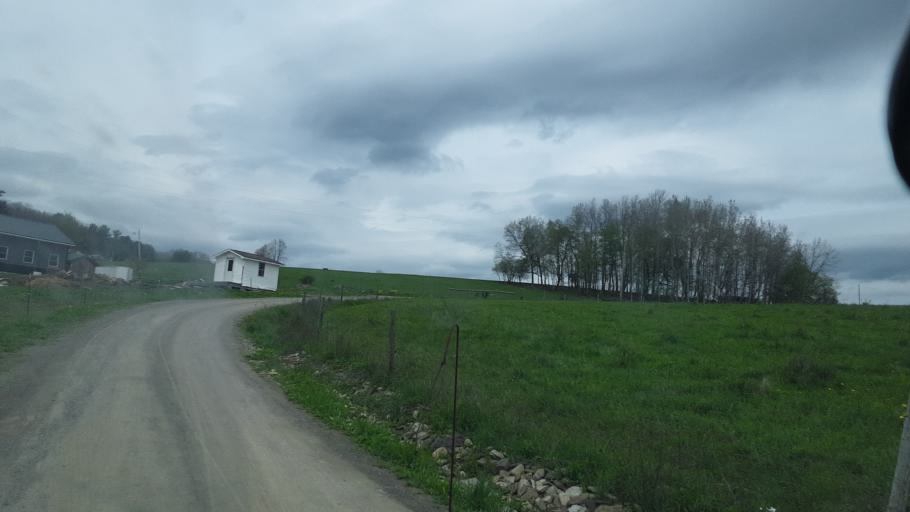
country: US
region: New York
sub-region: Steuben County
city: Addison
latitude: 42.0983
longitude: -77.2617
